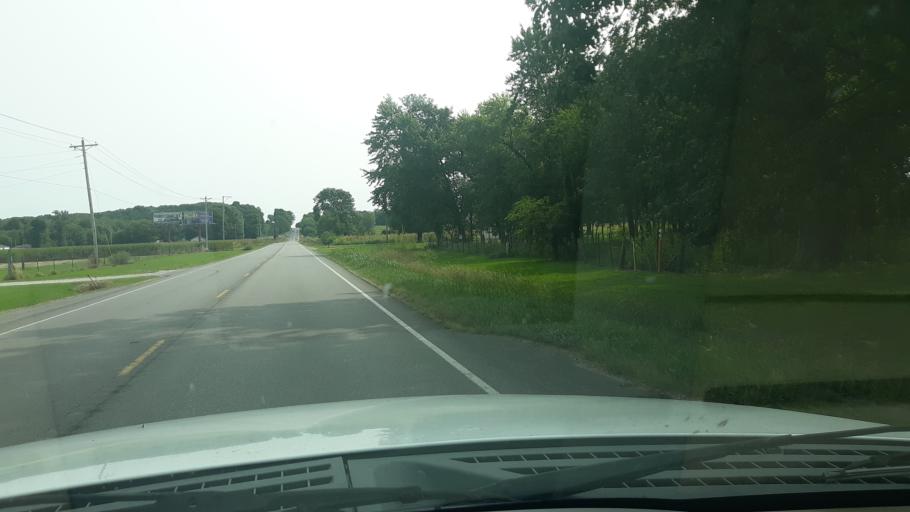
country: US
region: Indiana
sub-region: Gibson County
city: Owensville
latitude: 38.3559
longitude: -87.6690
